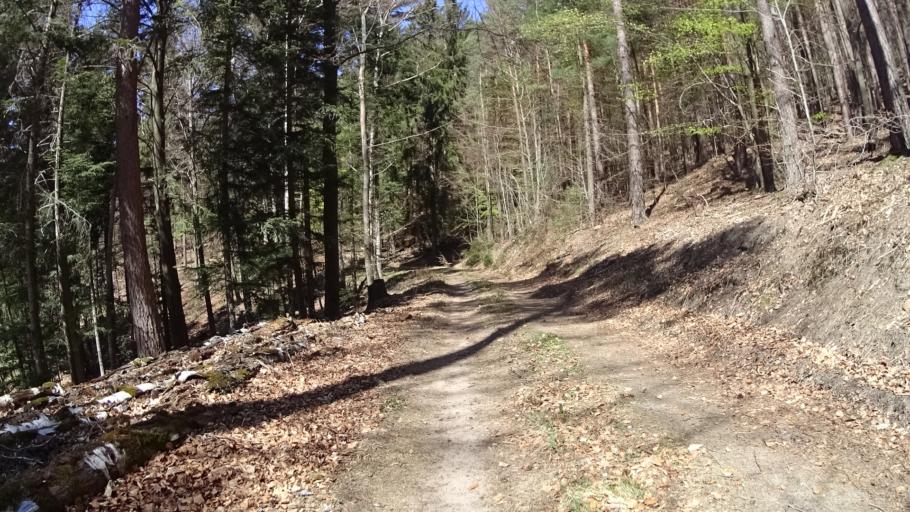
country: DE
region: Rheinland-Pfalz
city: Neidenfels
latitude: 49.4185
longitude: 8.0493
